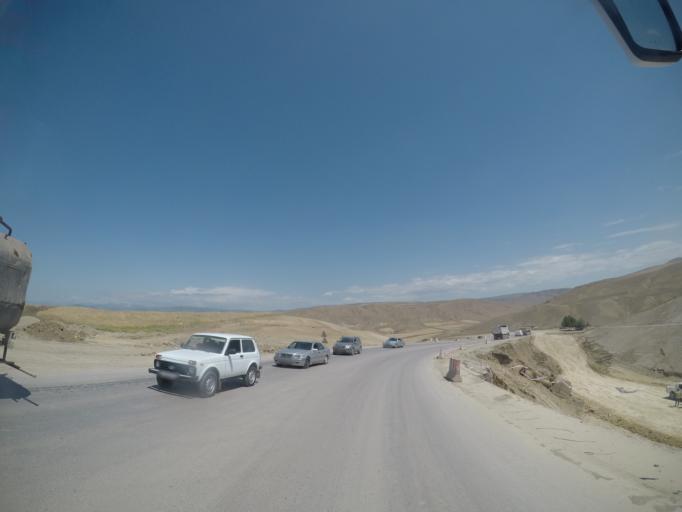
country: AZ
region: Samaxi
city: Shamakhi
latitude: 40.5465
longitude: 48.7710
